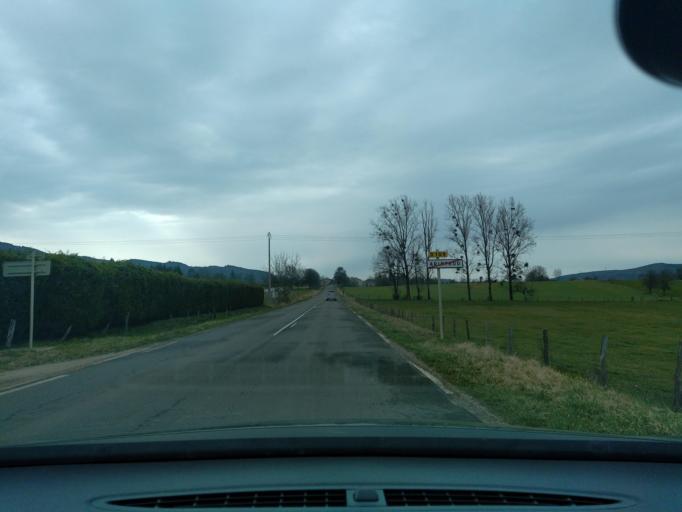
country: FR
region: Franche-Comte
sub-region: Departement du Jura
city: Arinthod
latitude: 46.3871
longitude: 5.5643
